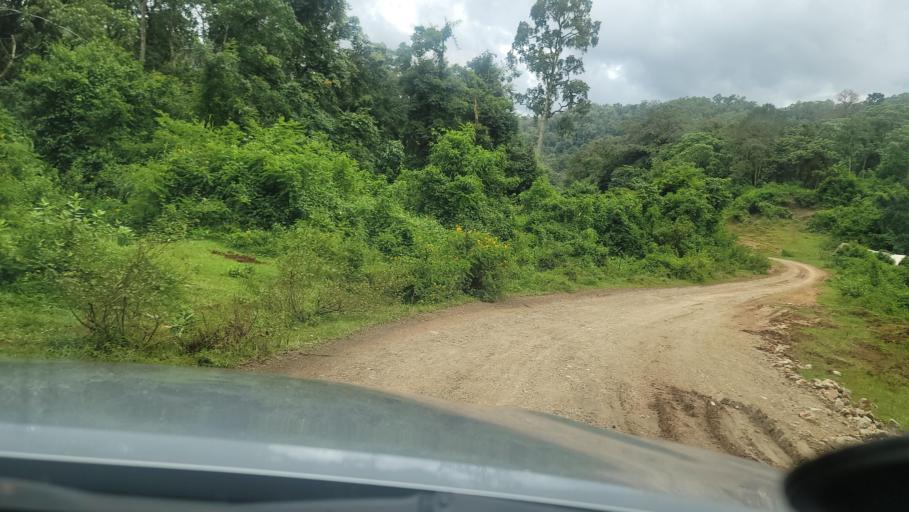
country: ET
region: Southern Nations, Nationalities, and People's Region
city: Bonga
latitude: 7.6169
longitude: 36.2080
